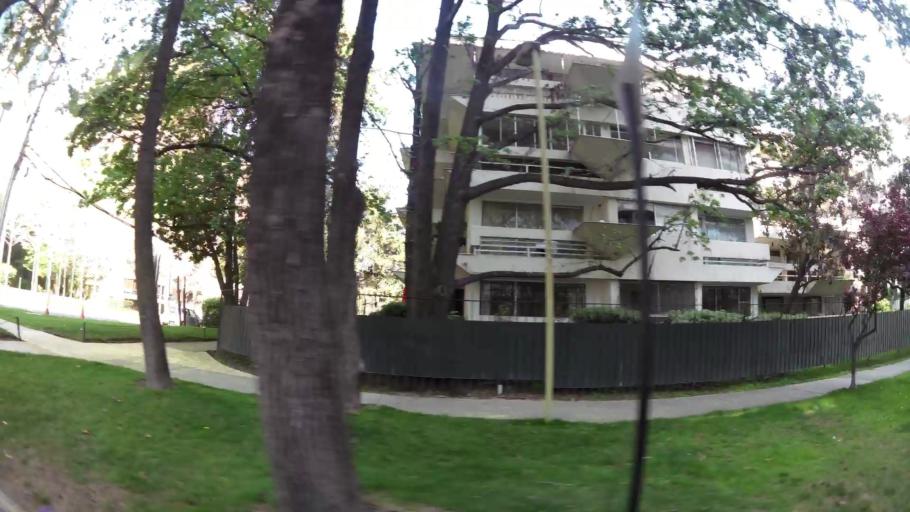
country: CL
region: Santiago Metropolitan
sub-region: Provincia de Santiago
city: Villa Presidente Frei, Nunoa, Santiago, Chile
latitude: -33.4174
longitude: -70.5893
